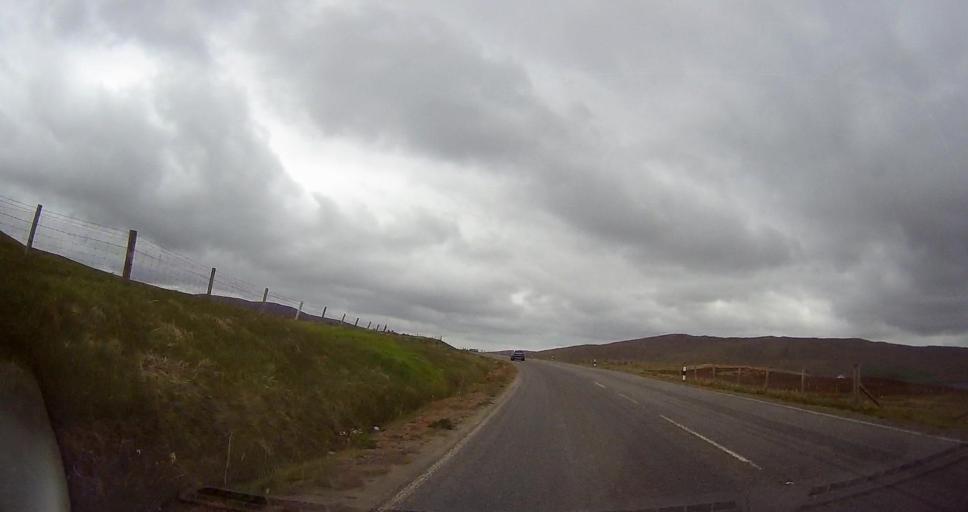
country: GB
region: Scotland
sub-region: Shetland Islands
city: Lerwick
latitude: 60.3723
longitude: -1.3348
